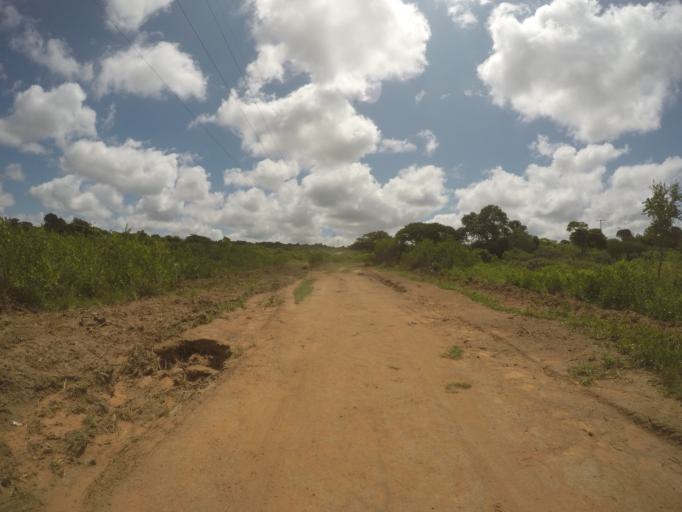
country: ZA
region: KwaZulu-Natal
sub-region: uThungulu District Municipality
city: Empangeni
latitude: -28.5888
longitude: 31.8379
